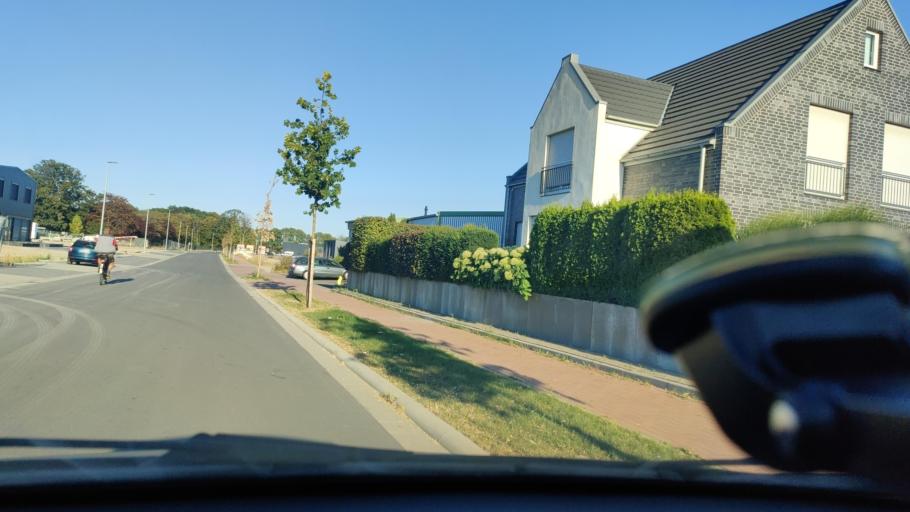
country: DE
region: North Rhine-Westphalia
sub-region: Regierungsbezirk Munster
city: Raesfeld
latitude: 51.7782
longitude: 6.8327
